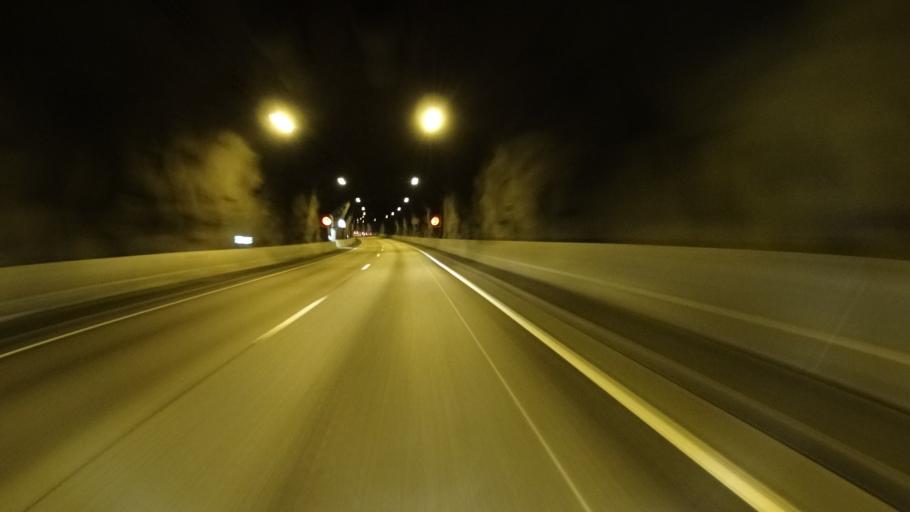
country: FI
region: Uusimaa
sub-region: Helsinki
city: Vantaa
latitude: 60.2286
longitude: 25.1631
